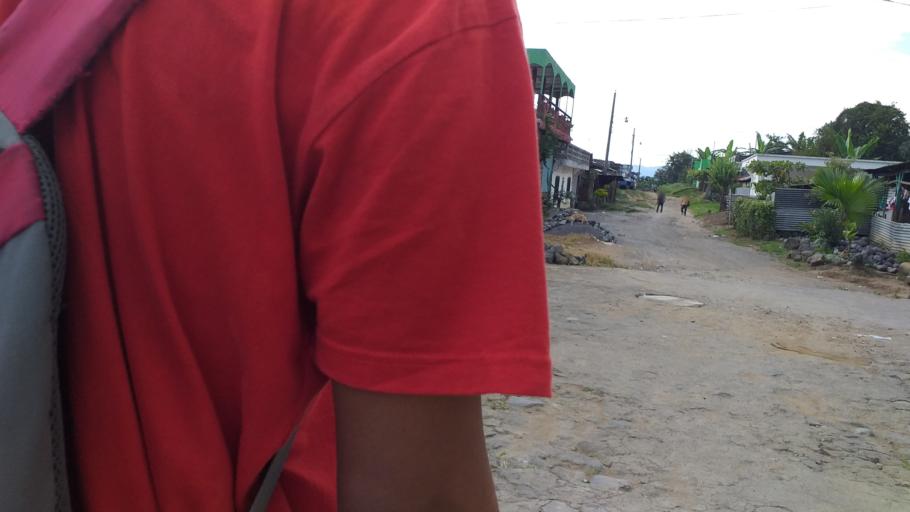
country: GT
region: Quetzaltenango
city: El Palmar
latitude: 14.6437
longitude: -91.5597
